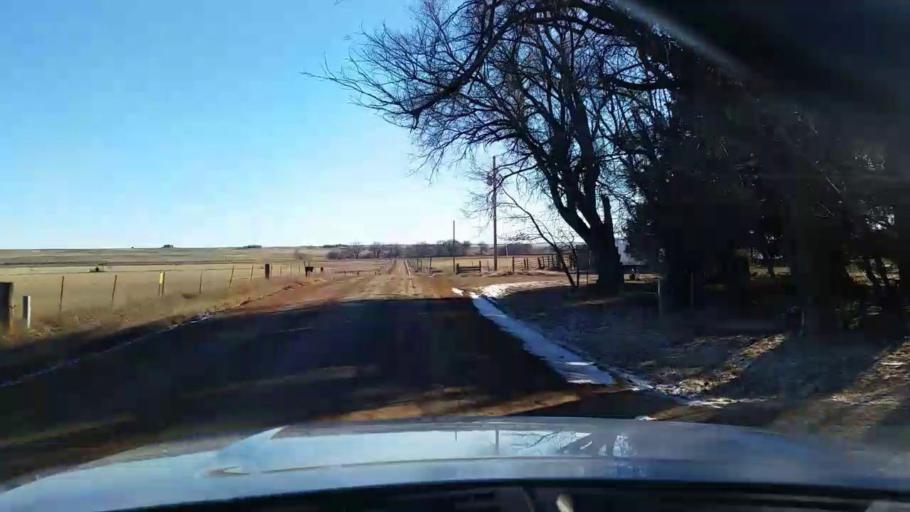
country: US
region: Colorado
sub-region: Larimer County
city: Wellington
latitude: 40.7694
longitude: -105.0475
